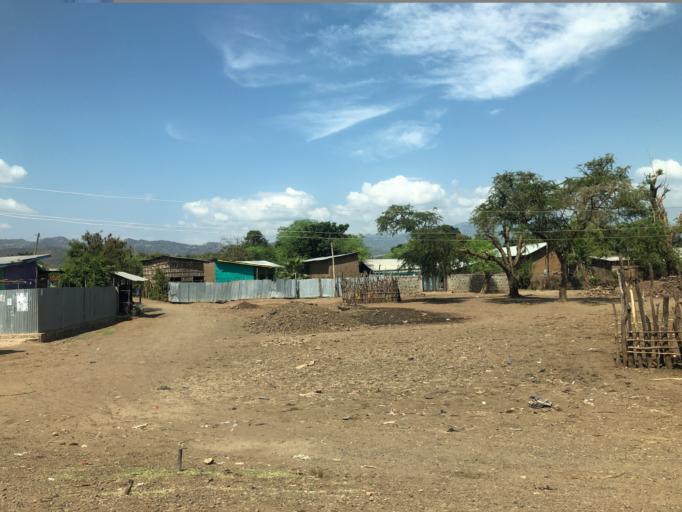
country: ET
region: Southern Nations, Nationalities, and People's Region
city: Arba Minch'
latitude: 5.8424
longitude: 37.4630
